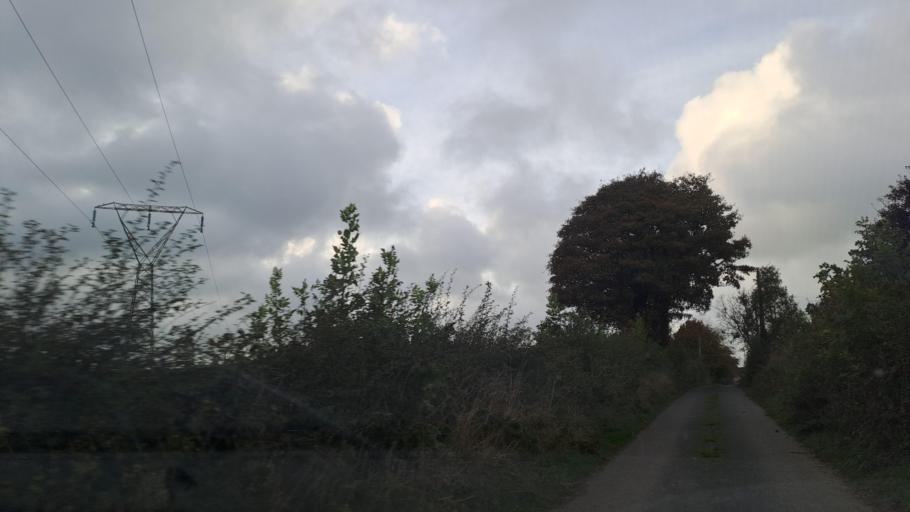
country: IE
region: Ulster
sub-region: County Monaghan
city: Carrickmacross
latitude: 54.0193
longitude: -6.7628
